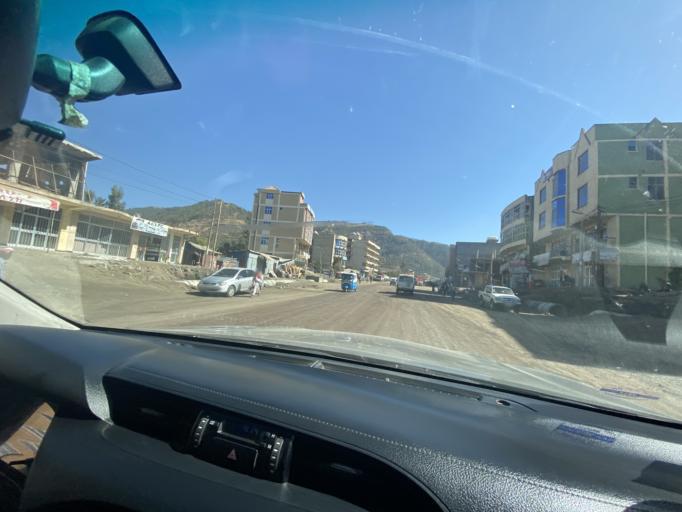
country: ET
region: Amhara
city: Robit
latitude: 11.8303
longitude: 39.6001
